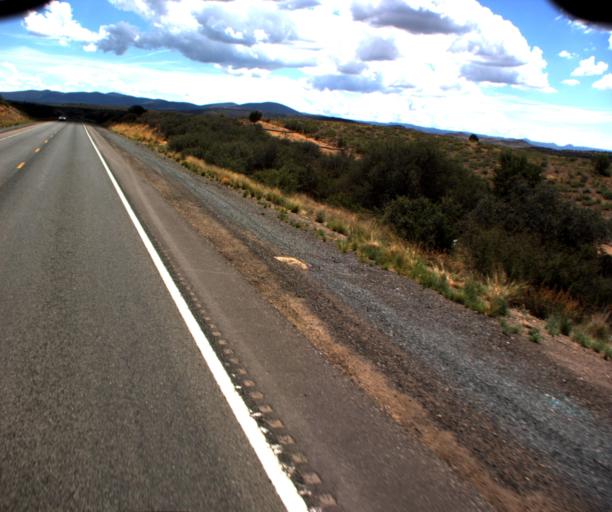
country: US
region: Arizona
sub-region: Yavapai County
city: Dewey-Humboldt
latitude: 34.5232
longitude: -112.0748
